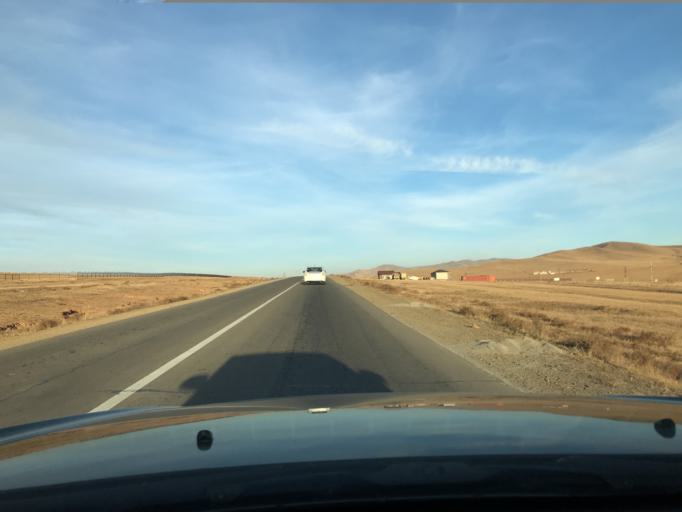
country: MN
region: Central Aimak
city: Arhust
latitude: 47.7970
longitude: 107.5046
